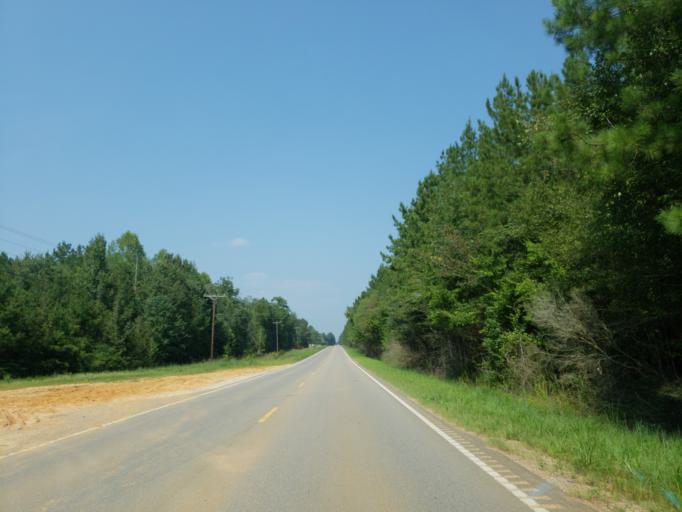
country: US
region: Mississippi
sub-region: Jones County
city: Ellisville
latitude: 31.5572
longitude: -89.2471
